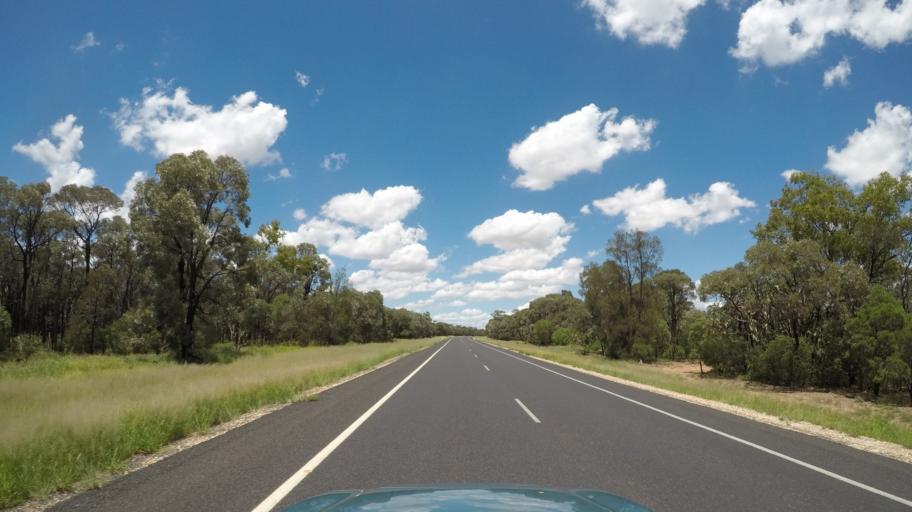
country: AU
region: Queensland
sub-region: Goondiwindi
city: Goondiwindi
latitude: -28.1040
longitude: 150.7227
